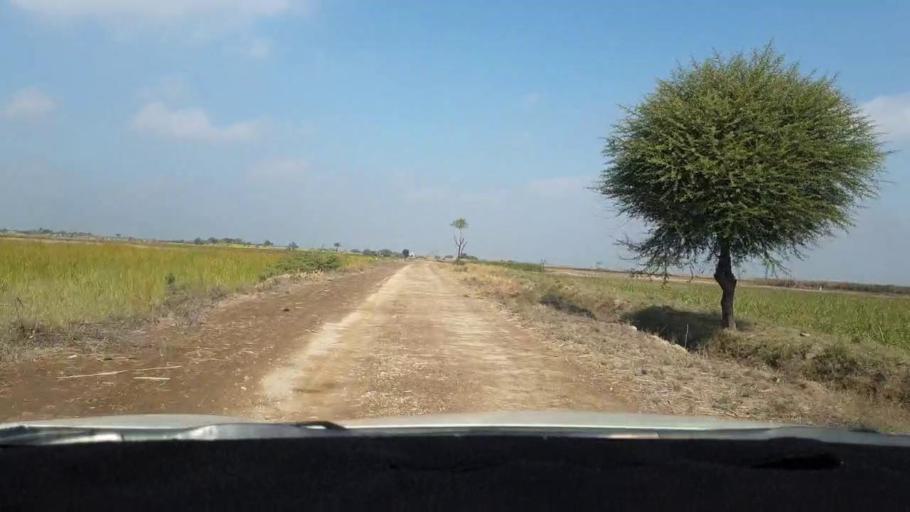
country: PK
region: Sindh
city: Berani
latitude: 25.7449
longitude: 69.0077
